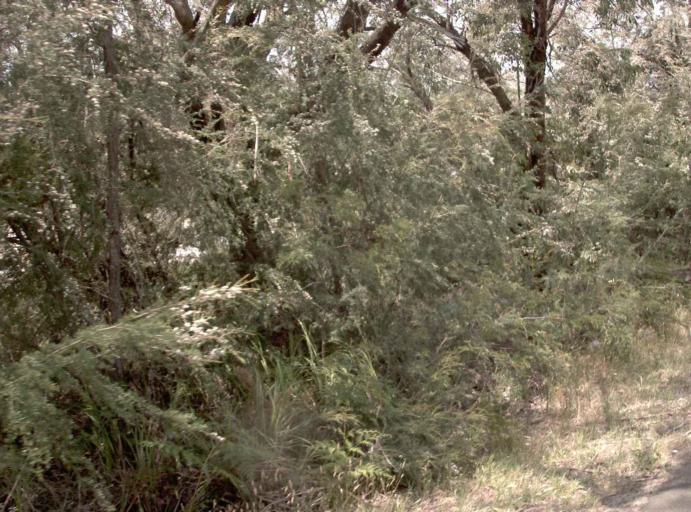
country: AU
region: Victoria
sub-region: Latrobe
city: Traralgon
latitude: -38.2716
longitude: 146.6922
